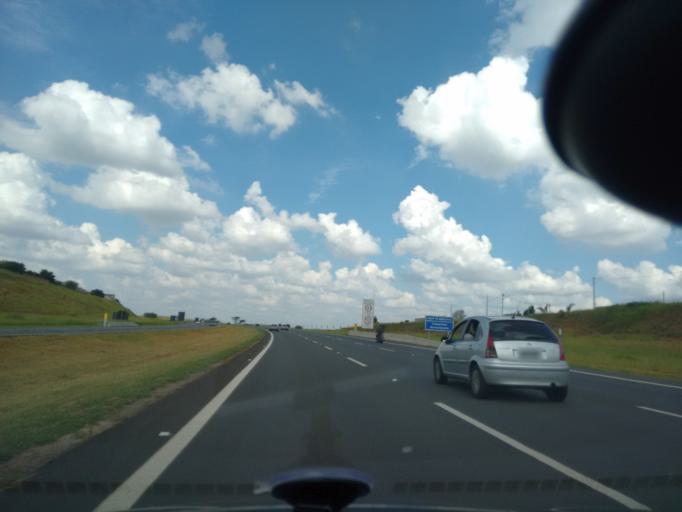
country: BR
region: Sao Paulo
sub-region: Hortolandia
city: Hortolandia
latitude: -22.9103
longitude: -47.1947
